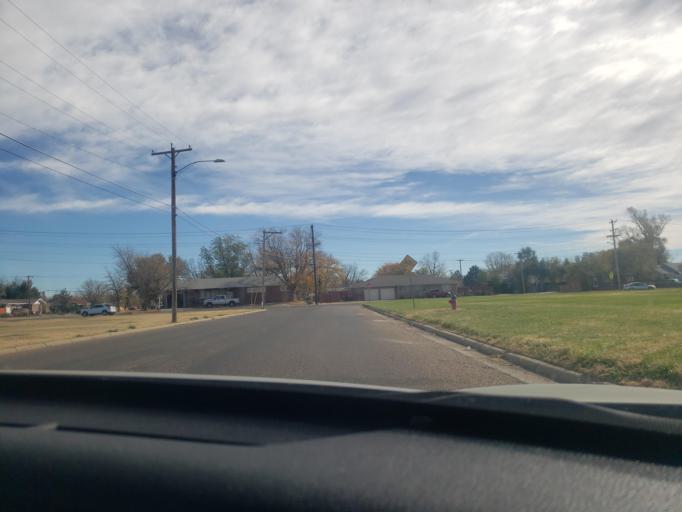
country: US
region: Kansas
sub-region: Finney County
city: Garden City
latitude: 37.9788
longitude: -100.8664
